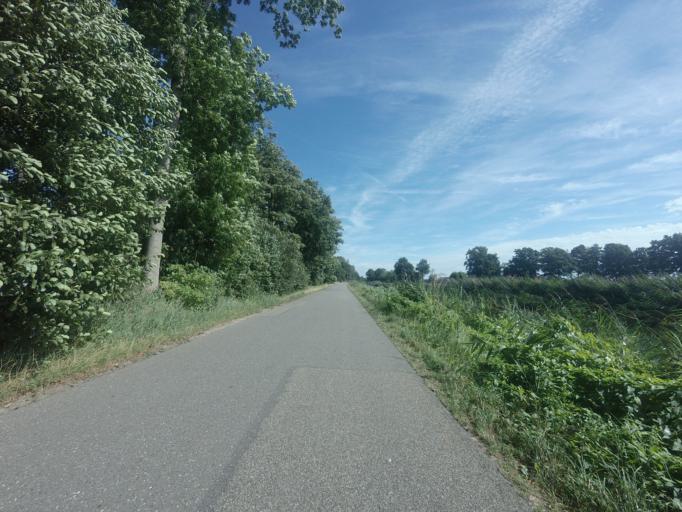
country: NL
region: Overijssel
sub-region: Gemeente Raalte
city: Raalte
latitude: 52.4041
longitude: 6.3006
